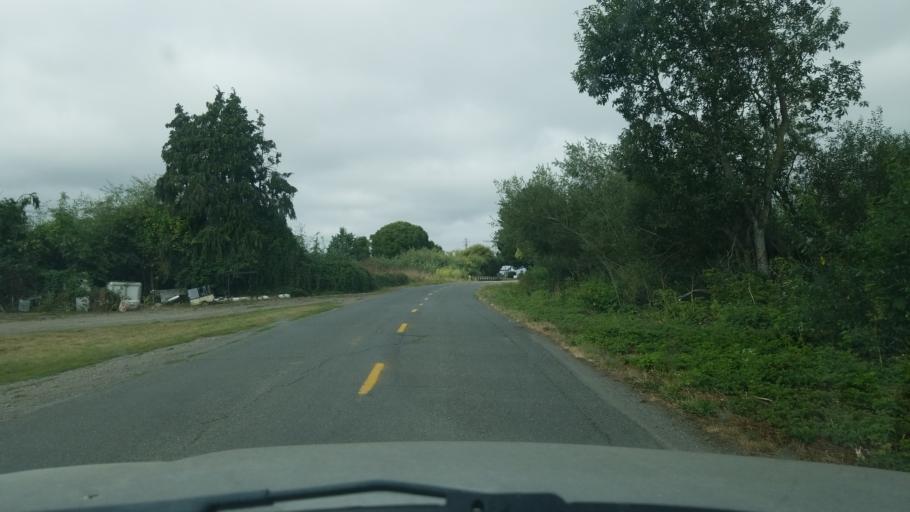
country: US
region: California
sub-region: Humboldt County
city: Ferndale
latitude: 40.5944
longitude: -124.2520
